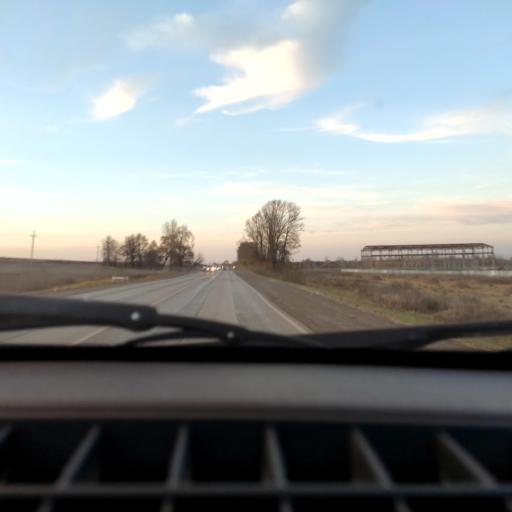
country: RU
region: Bashkortostan
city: Avdon
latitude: 54.7238
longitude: 55.8077
